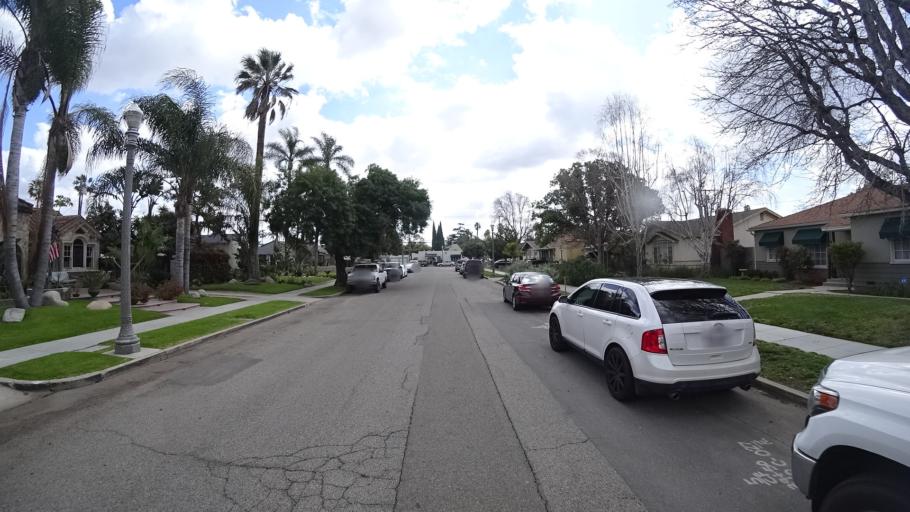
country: US
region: California
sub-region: Orange County
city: Anaheim
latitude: 33.8444
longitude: -117.9200
